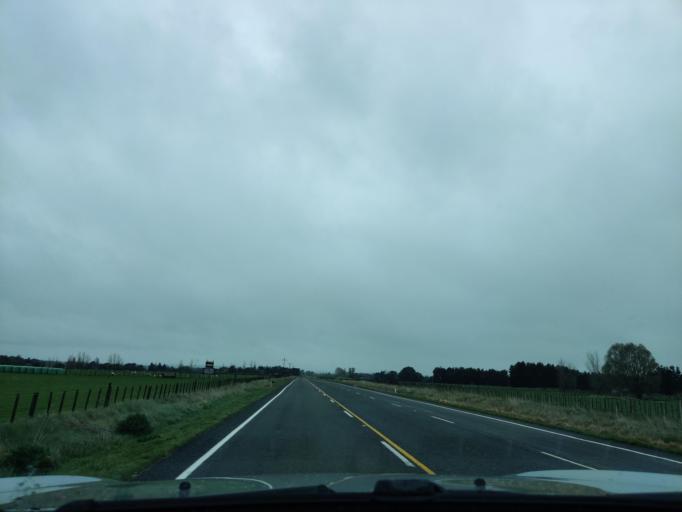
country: NZ
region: Hawke's Bay
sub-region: Hastings District
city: Hastings
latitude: -40.0208
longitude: 176.3081
